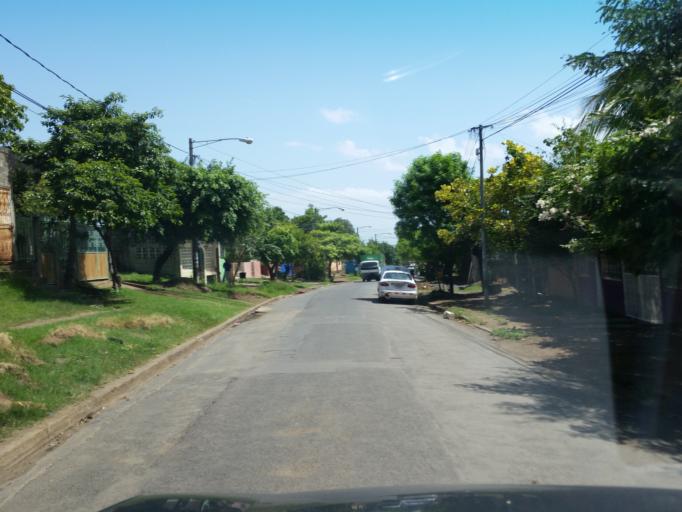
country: NI
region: Managua
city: Managua
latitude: 12.1170
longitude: -86.2075
